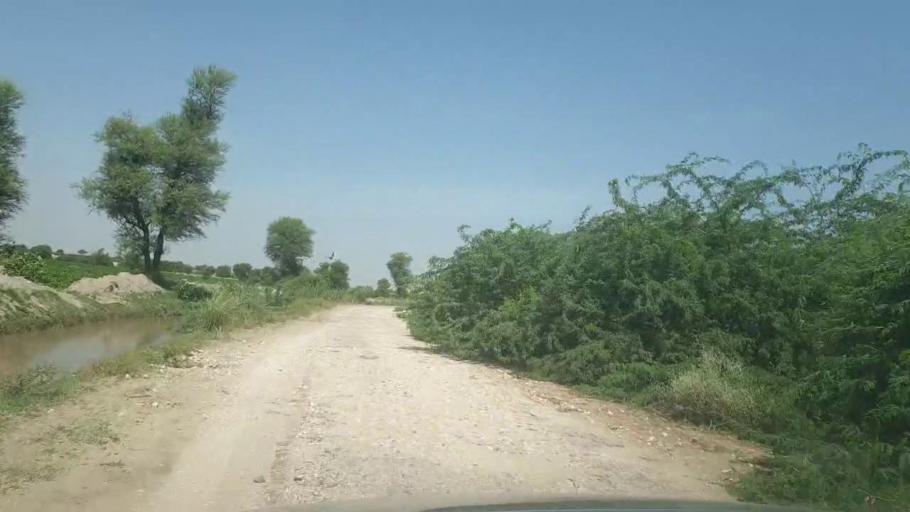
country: PK
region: Sindh
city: Khairpur
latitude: 27.4005
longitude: 69.0394
